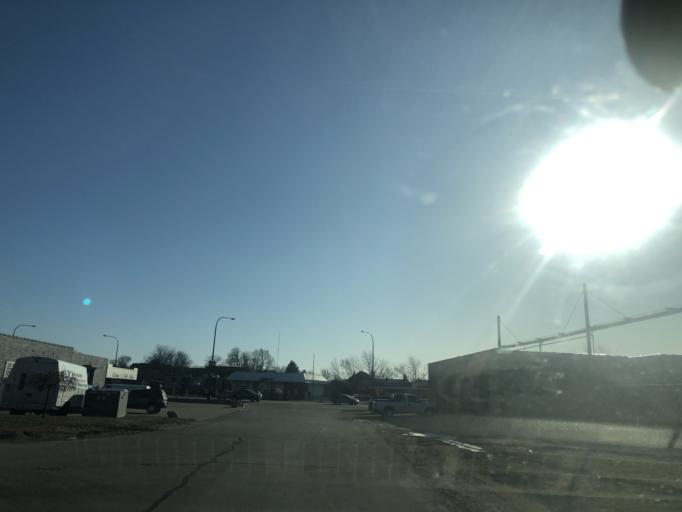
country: US
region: Illinois
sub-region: DuPage County
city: Addison
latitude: 41.9412
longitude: -88.0077
